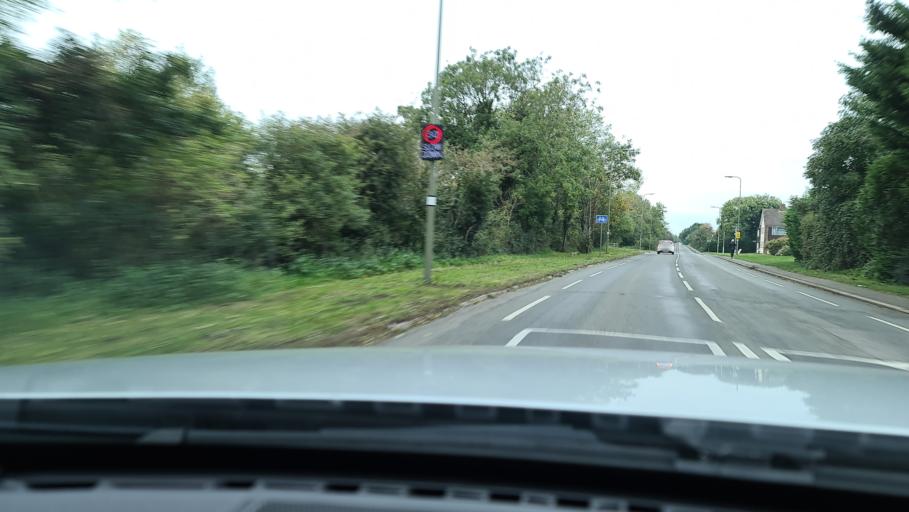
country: GB
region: England
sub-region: Oxfordshire
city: Bicester
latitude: 51.8962
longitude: -1.1627
